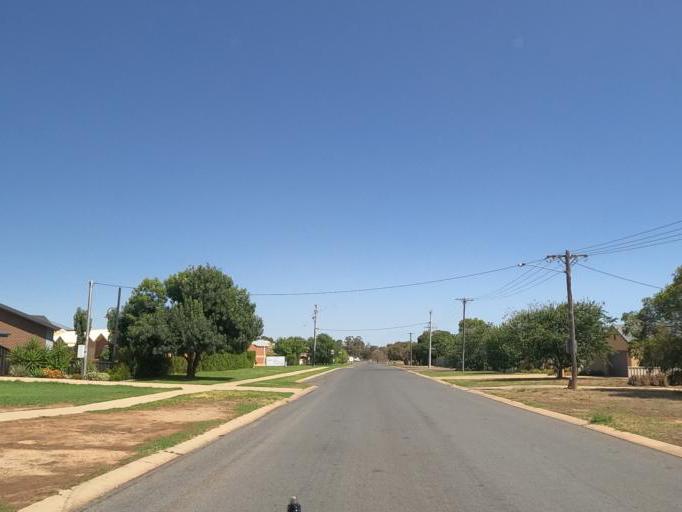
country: AU
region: New South Wales
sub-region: Corowa Shire
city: Mulwala
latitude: -35.9862
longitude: 146.0041
